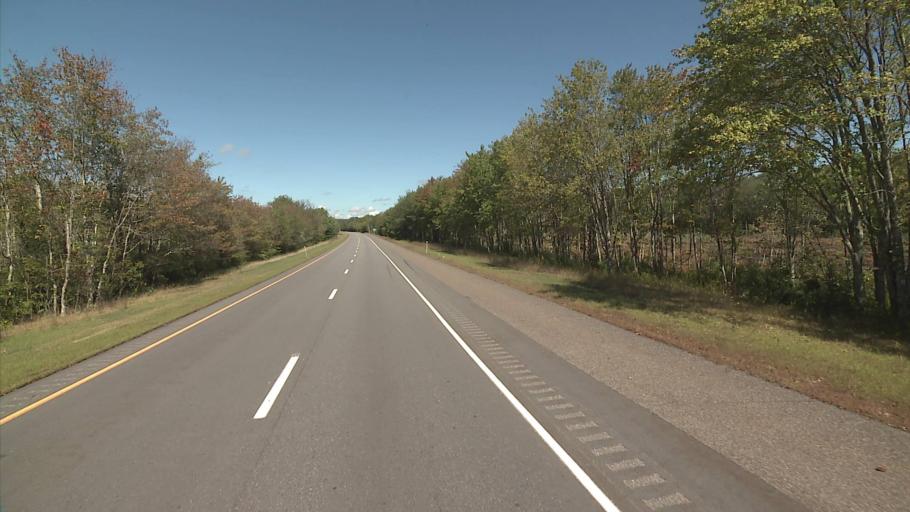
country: US
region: Connecticut
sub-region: New London County
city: Colchester
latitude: 41.5184
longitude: -72.3029
